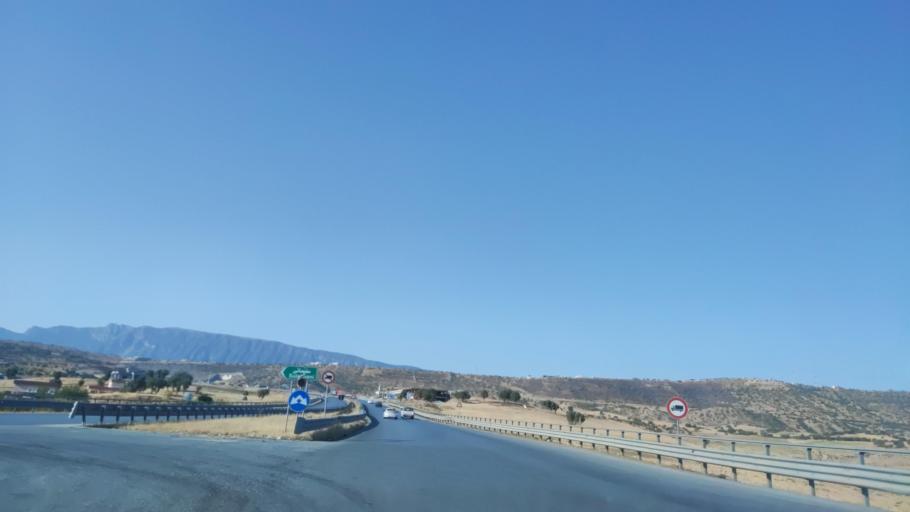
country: IQ
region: Arbil
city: Shaqlawah
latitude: 36.4522
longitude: 44.3798
